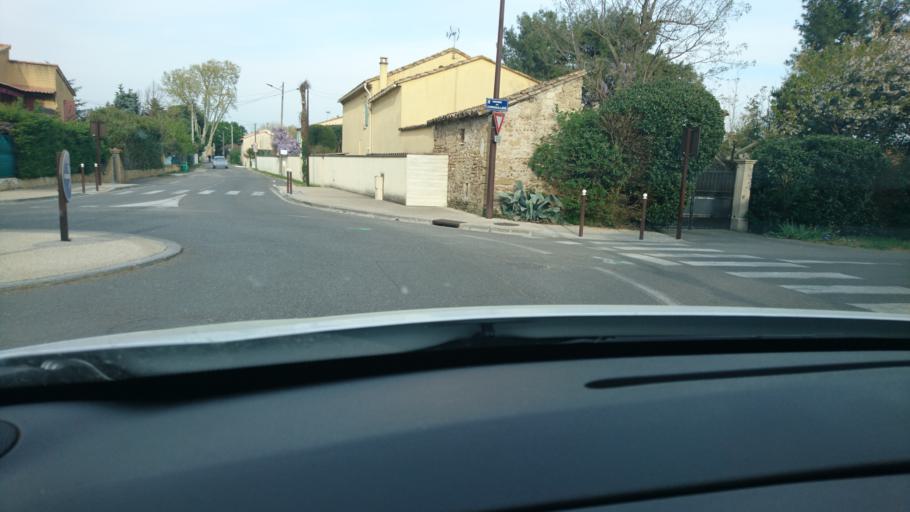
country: FR
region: Provence-Alpes-Cote d'Azur
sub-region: Departement du Vaucluse
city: Montfavet
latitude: 43.9306
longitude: 4.8816
